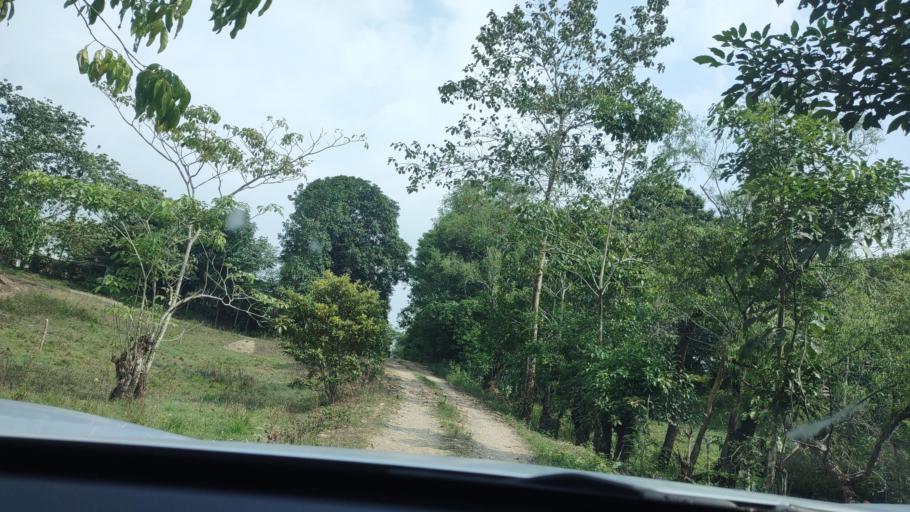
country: MX
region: Veracruz
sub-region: Uxpanapa
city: Poblado 10
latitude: 17.5453
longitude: -94.2913
